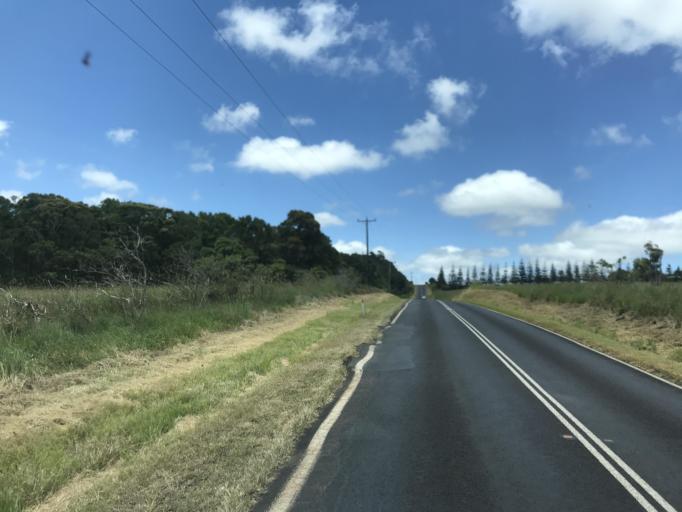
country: AU
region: Queensland
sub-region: Tablelands
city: Ravenshoe
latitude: -17.5030
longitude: 145.4764
